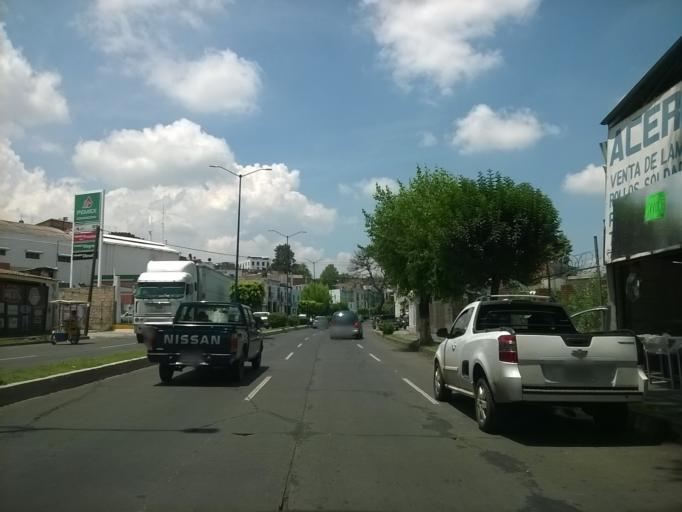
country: MX
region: Michoacan
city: Morelia
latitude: 19.7088
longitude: -101.1915
